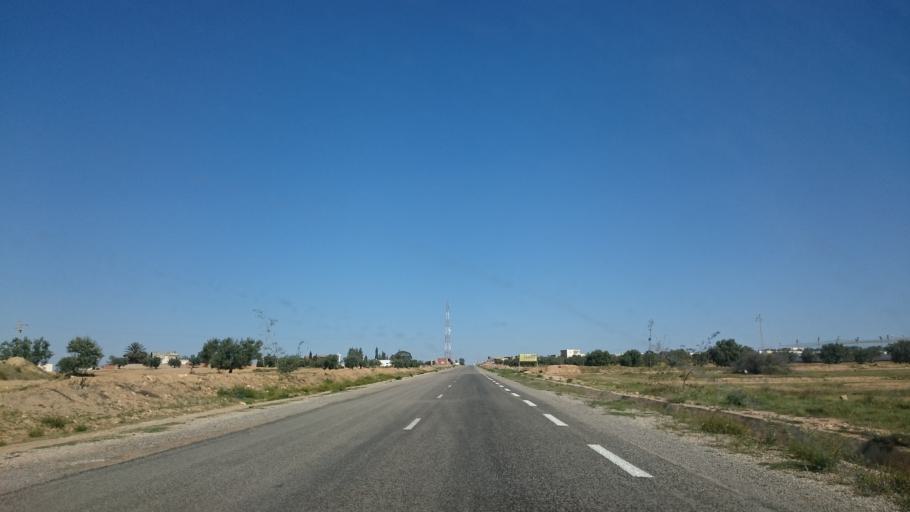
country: TN
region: Safaqis
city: Sfax
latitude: 34.8104
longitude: 10.4797
